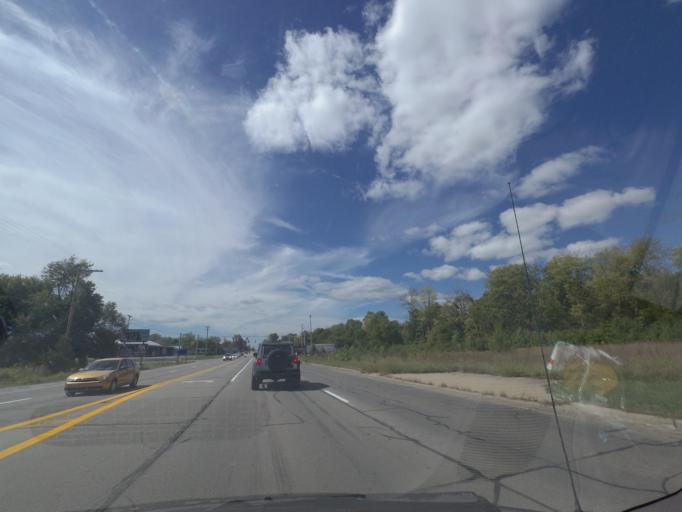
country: US
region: Indiana
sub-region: Hancock County
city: Greenfield
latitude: 39.7820
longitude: -85.8383
